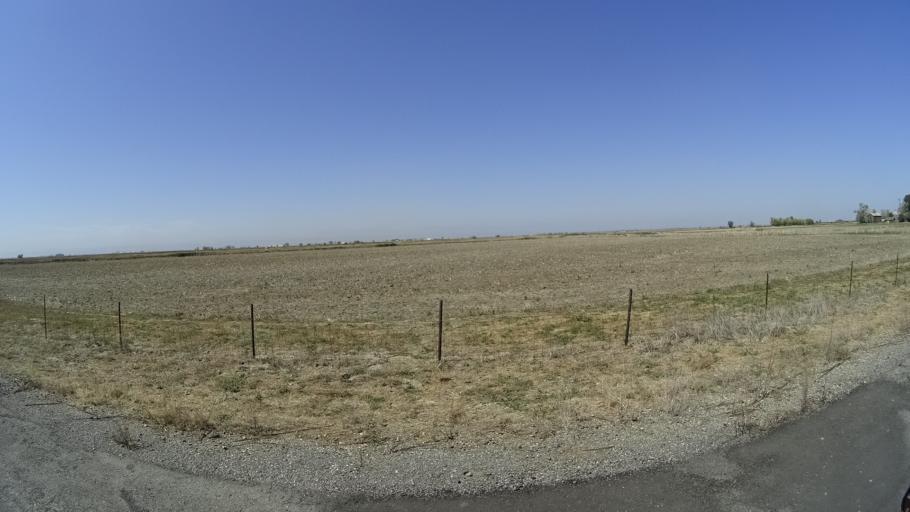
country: US
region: California
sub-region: Glenn County
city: Willows
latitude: 39.4955
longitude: -122.0933
